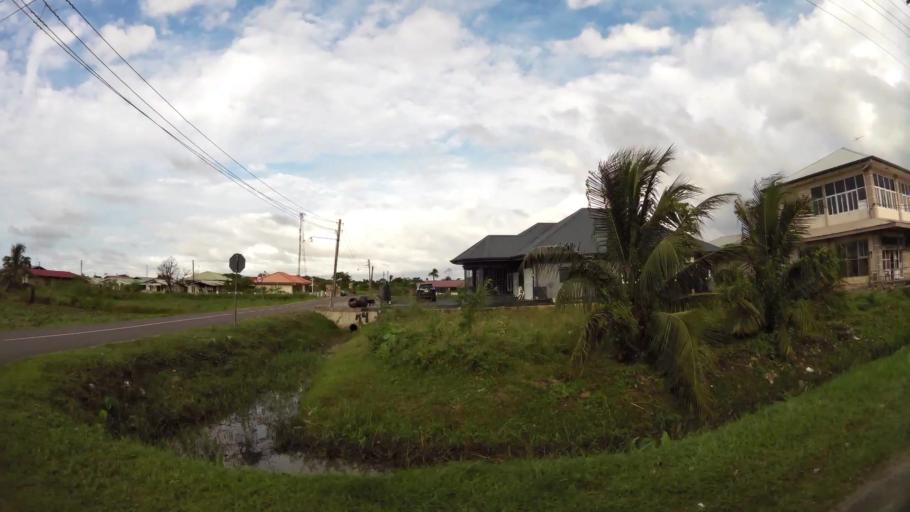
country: SR
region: Paramaribo
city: Paramaribo
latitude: 5.8427
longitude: -55.2655
